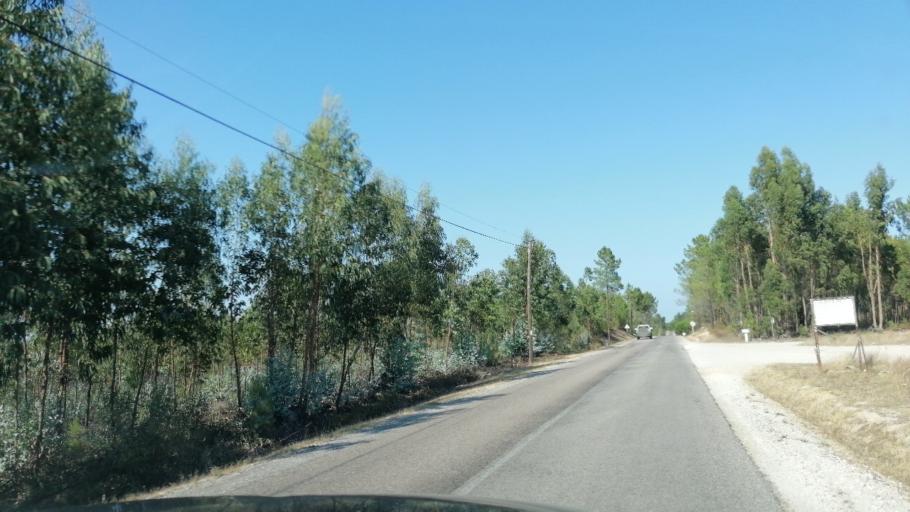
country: PT
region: Evora
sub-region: Vendas Novas
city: Vendas Novas
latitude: 38.7750
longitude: -8.5969
